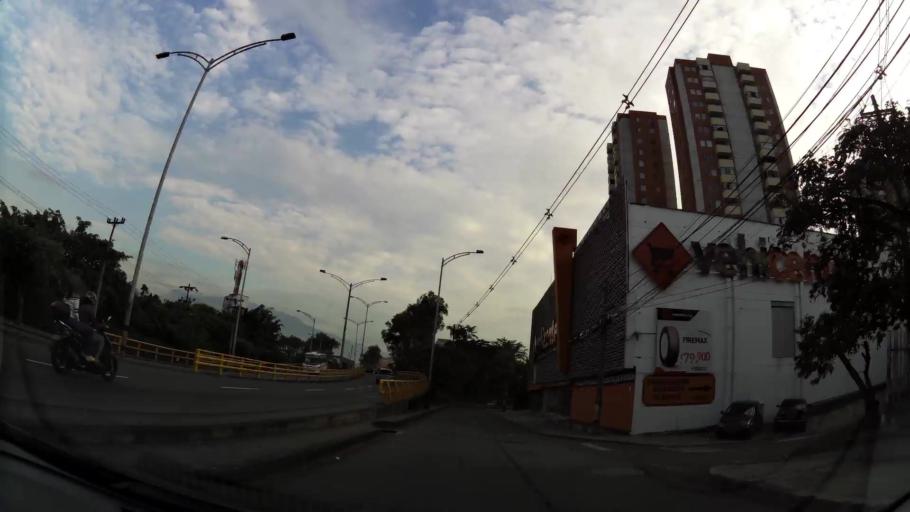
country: CO
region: Antioquia
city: Medellin
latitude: 6.2265
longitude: -75.5691
